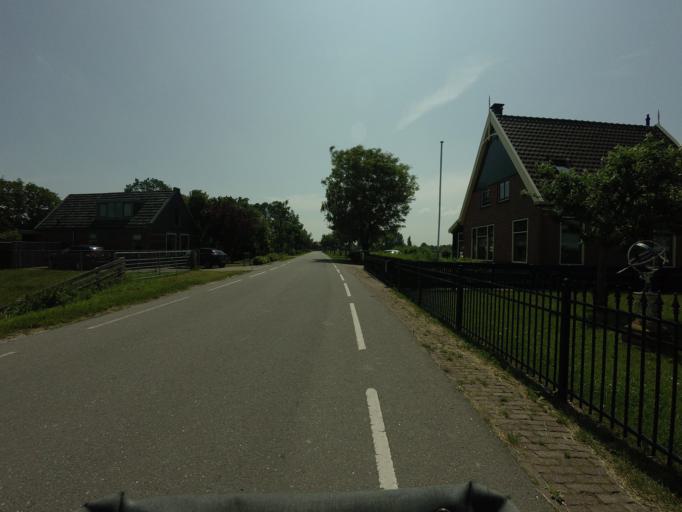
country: NL
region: North Holland
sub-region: Gemeente Opmeer
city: Opmeer
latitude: 52.6645
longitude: 4.9478
